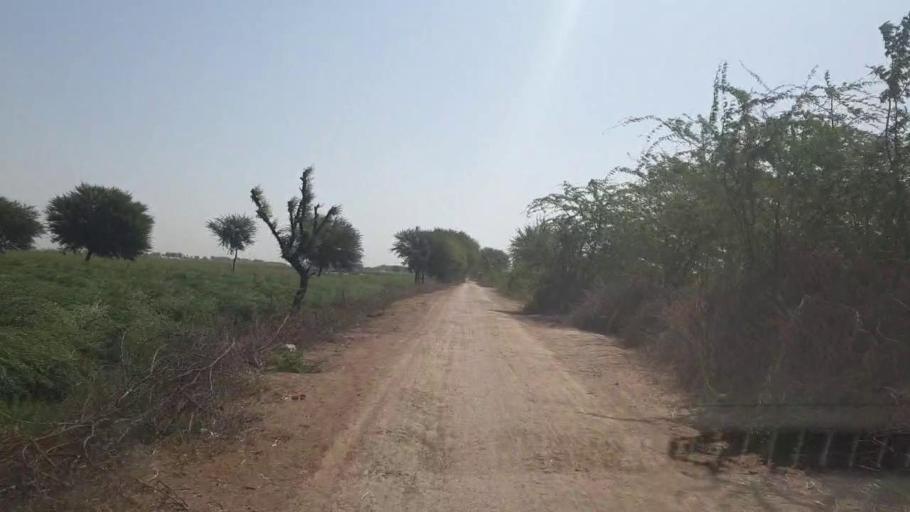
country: PK
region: Sindh
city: Kunri
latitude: 25.2740
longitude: 69.6292
